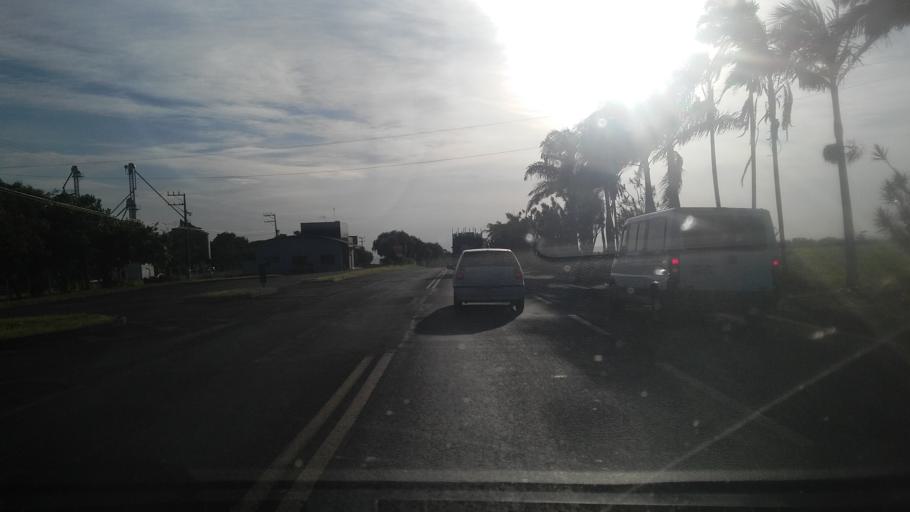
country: BR
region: Parana
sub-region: Bandeirantes
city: Bandeirantes
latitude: -23.1453
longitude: -50.5767
